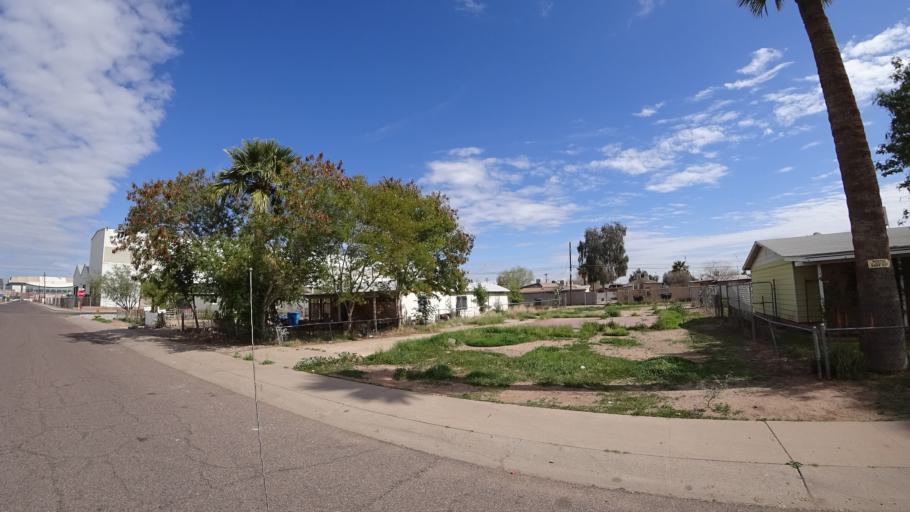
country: US
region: Arizona
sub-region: Maricopa County
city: Phoenix
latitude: 33.4325
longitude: -112.0674
